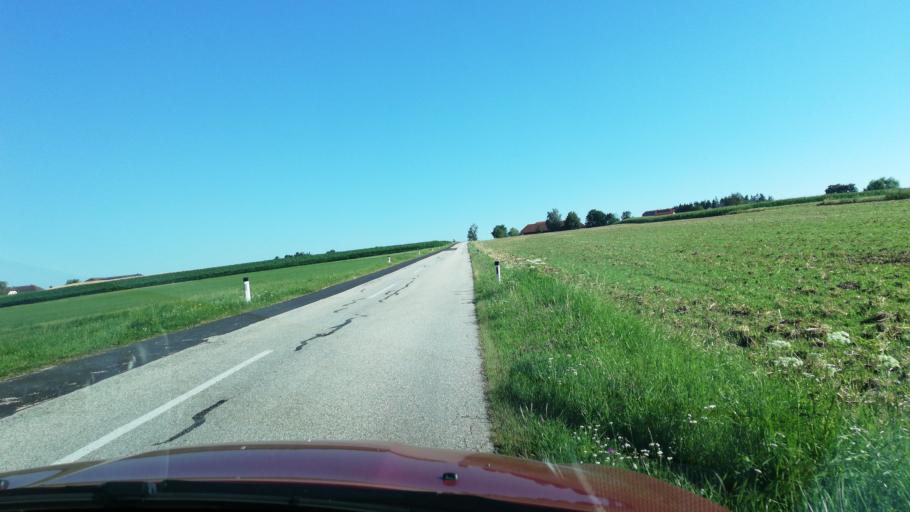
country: AT
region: Upper Austria
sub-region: Politischer Bezirk Rohrbach
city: Kleinzell im Muehlkreis
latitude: 48.4607
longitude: 14.0466
